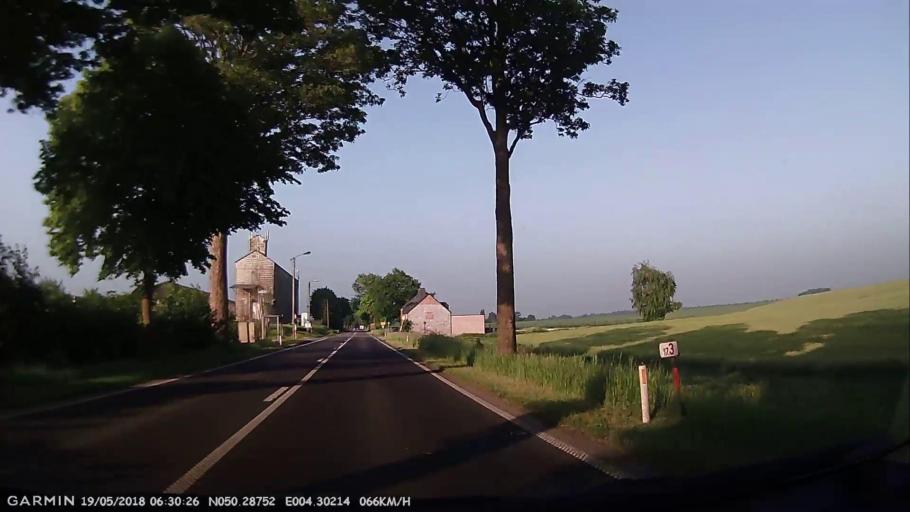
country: BE
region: Wallonia
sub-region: Province du Hainaut
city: Thuin
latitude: 50.2875
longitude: 4.3021
